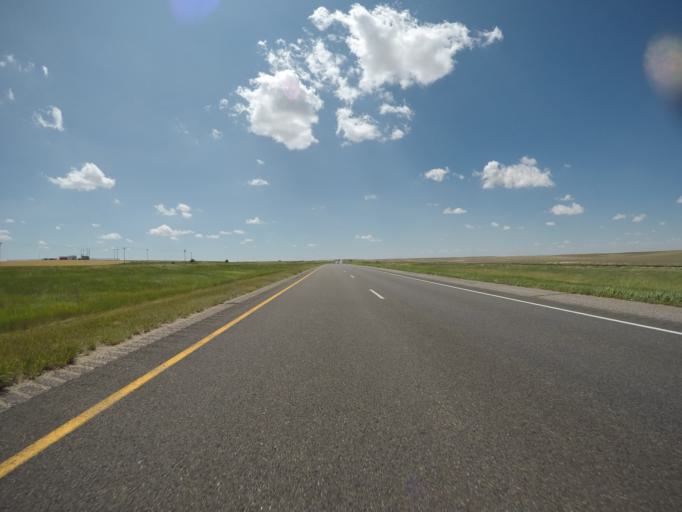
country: US
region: Colorado
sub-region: Lincoln County
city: Hugo
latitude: 39.2870
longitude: -103.1520
